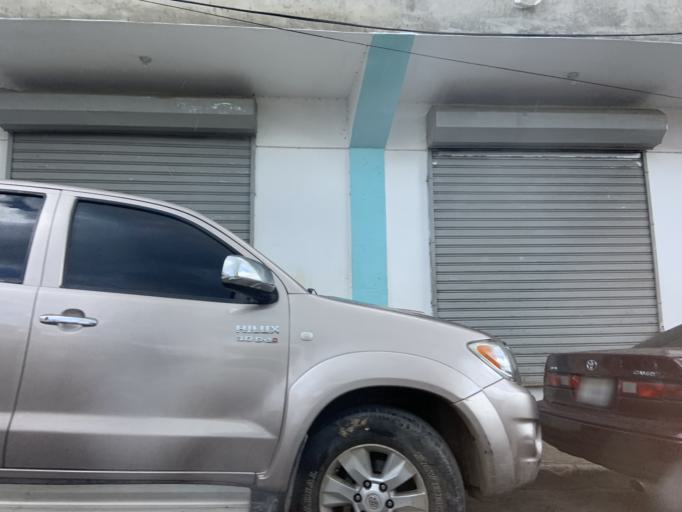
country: DO
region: Monte Plata
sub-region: Yamasa
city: Yamasa
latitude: 18.7746
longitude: -70.0266
